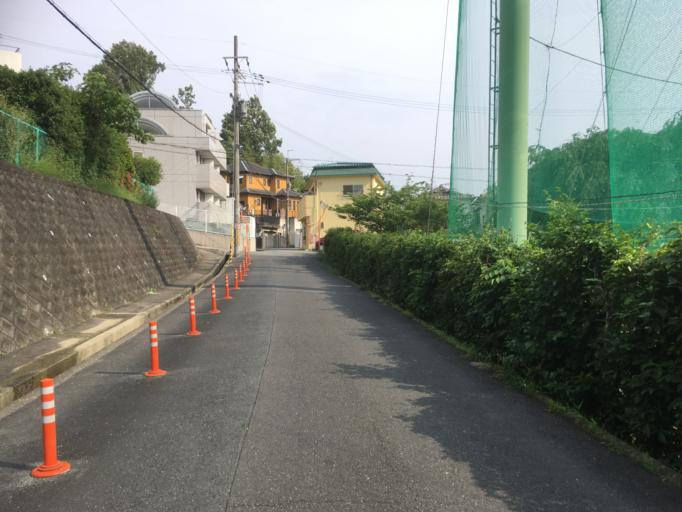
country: JP
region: Nara
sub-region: Ikoma-shi
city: Ikoma
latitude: 34.6986
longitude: 135.7008
